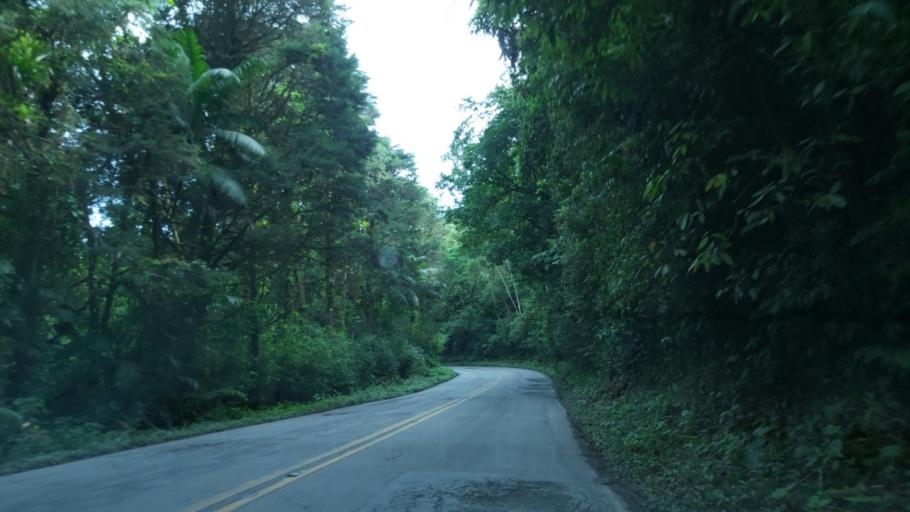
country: BR
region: Sao Paulo
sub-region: Miracatu
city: Miracatu
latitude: -24.0424
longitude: -47.5684
